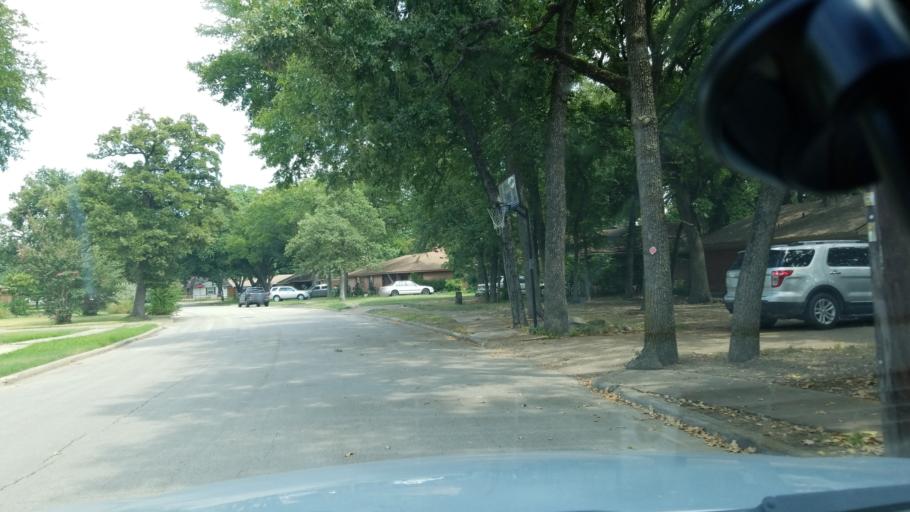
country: US
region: Texas
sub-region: Dallas County
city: Irving
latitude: 32.8194
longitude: -96.9808
